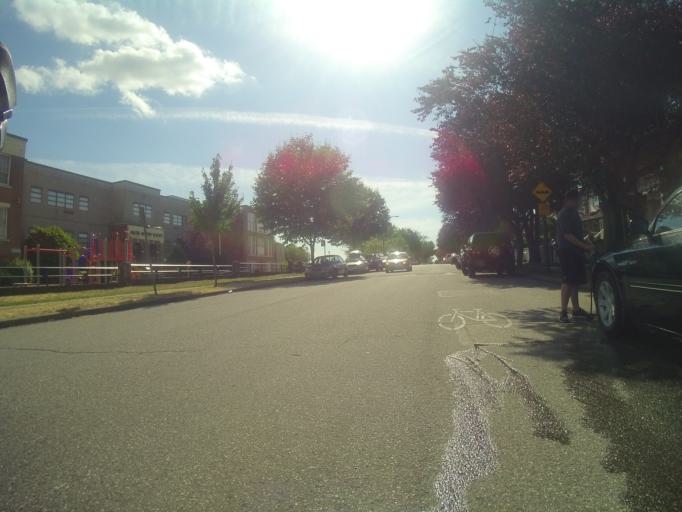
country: CA
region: British Columbia
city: Vancouver
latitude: 49.2165
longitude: -123.0832
